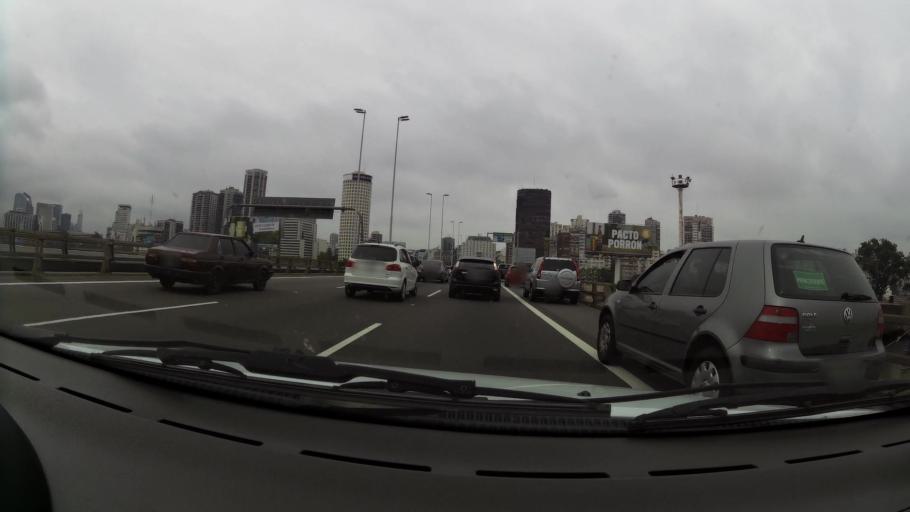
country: AR
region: Buenos Aires F.D.
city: Retiro
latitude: -34.5856
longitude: -58.3801
